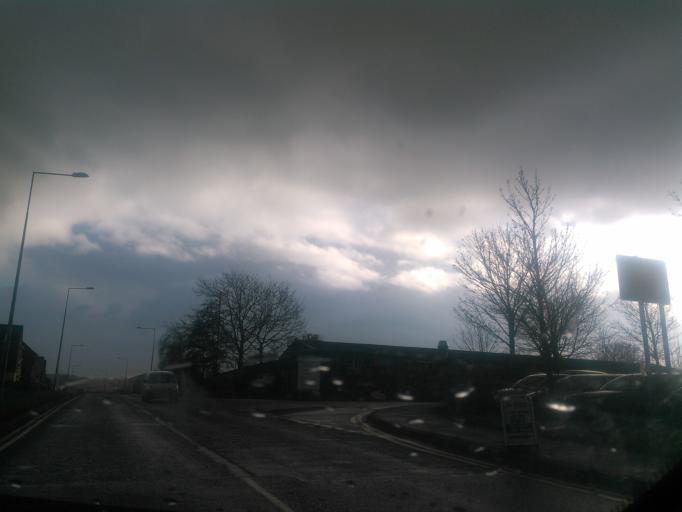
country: GB
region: England
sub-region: Shropshire
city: Hadley
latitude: 52.7084
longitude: -2.4719
